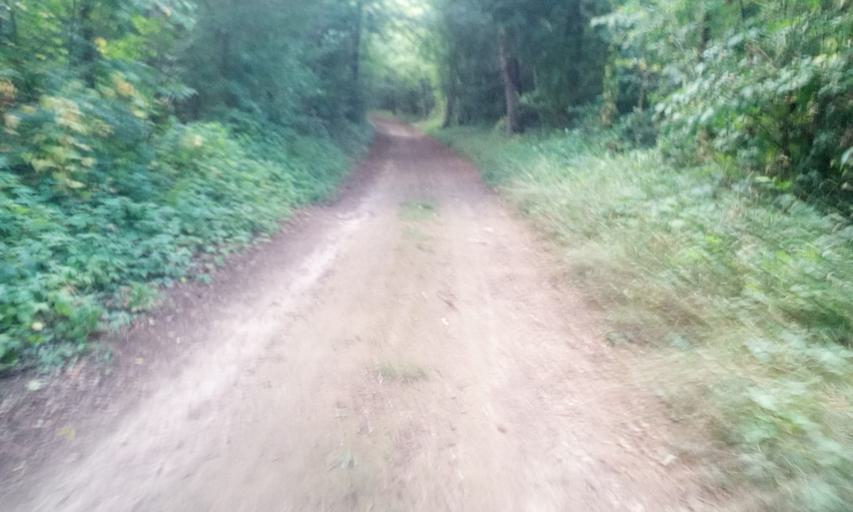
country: FR
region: Lower Normandy
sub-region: Departement du Calvados
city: Bellengreville
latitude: 49.1052
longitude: -0.2459
